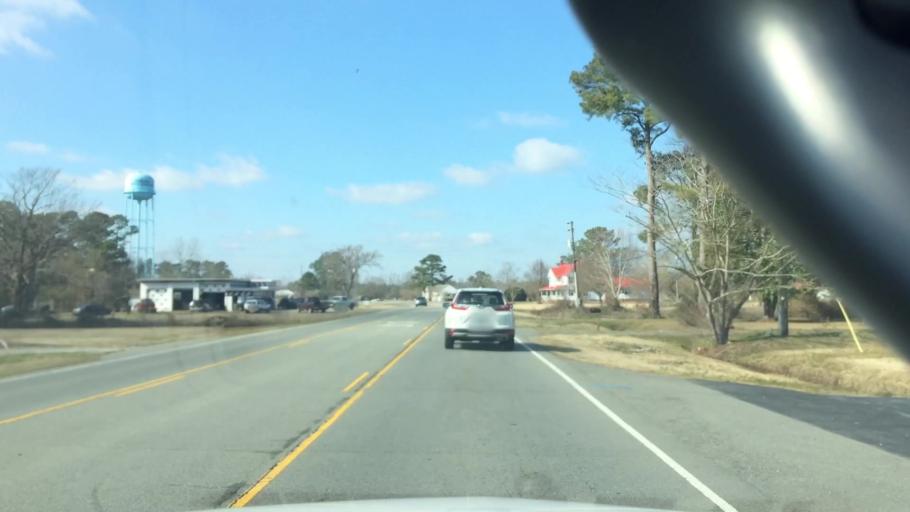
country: US
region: North Carolina
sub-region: Duplin County
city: Beulaville
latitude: 34.8324
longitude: -77.8211
